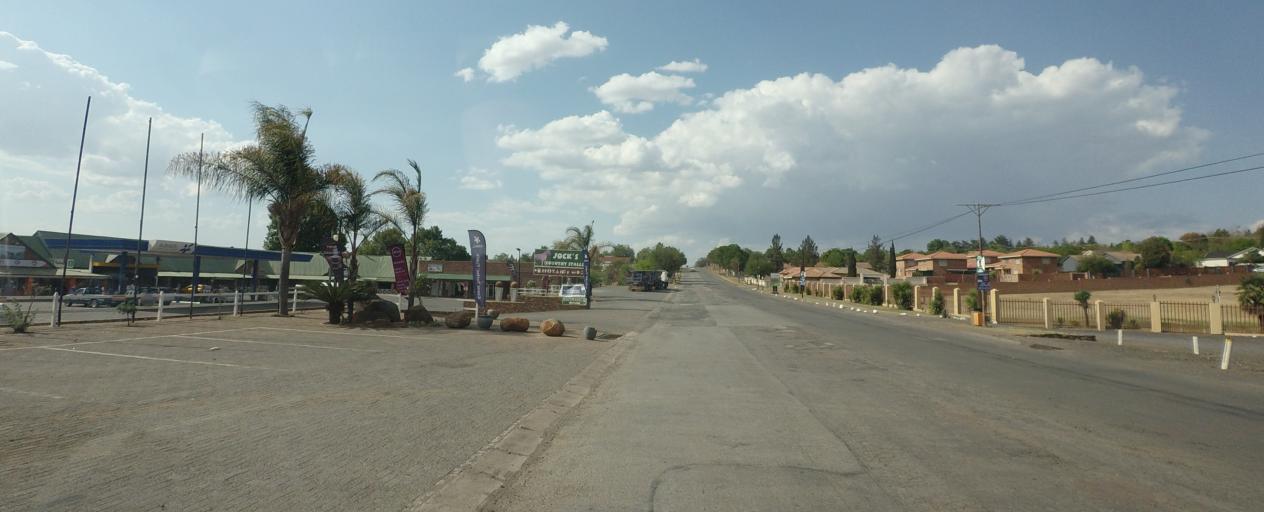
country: ZA
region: Mpumalanga
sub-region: Ehlanzeni District
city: Lydenburg
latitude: -25.1121
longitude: 30.4479
